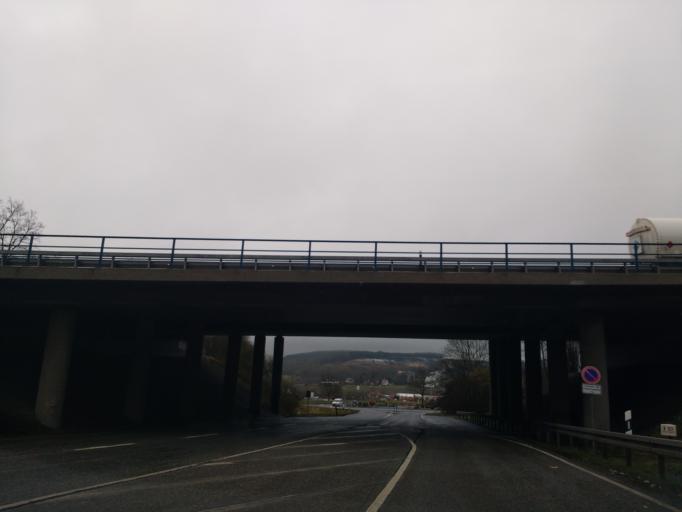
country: DE
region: Hesse
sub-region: Regierungsbezirk Kassel
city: Homberg
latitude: 51.0032
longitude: 9.4807
